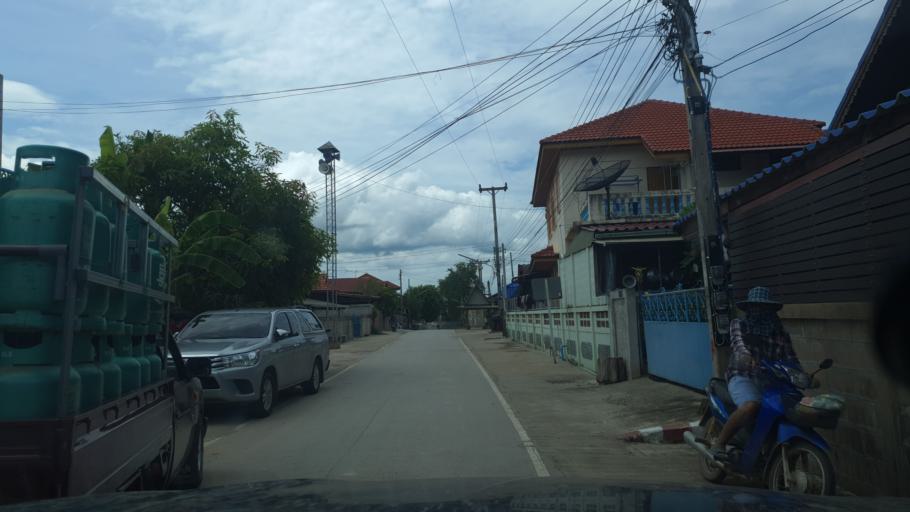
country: TH
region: Lampang
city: Sop Prap
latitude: 17.8795
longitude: 99.3834
